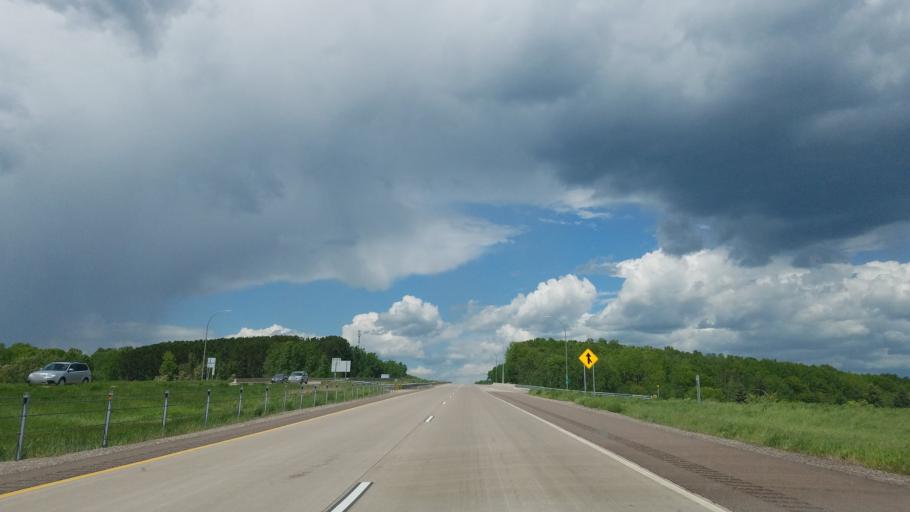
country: US
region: Minnesota
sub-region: Carlton County
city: Moose Lake
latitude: 46.4513
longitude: -92.7312
